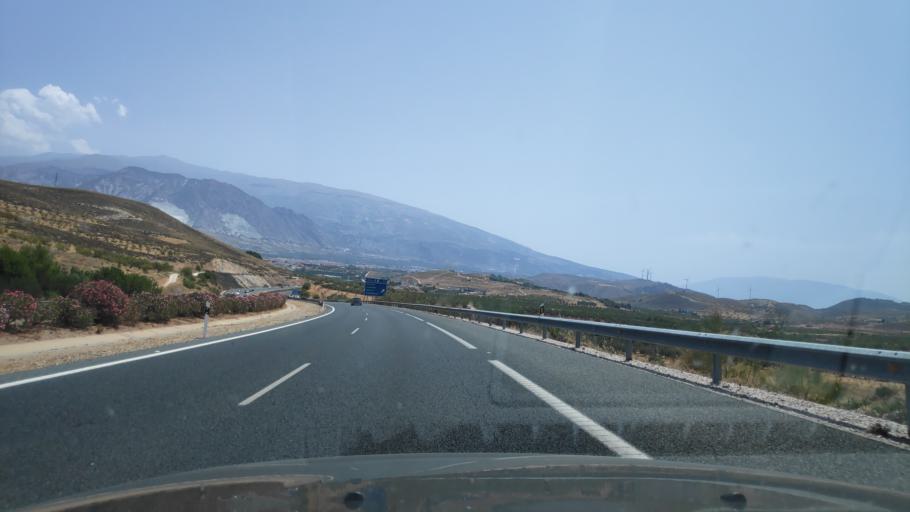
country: ES
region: Andalusia
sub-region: Provincia de Granada
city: Padul
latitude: 36.9912
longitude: -3.6231
